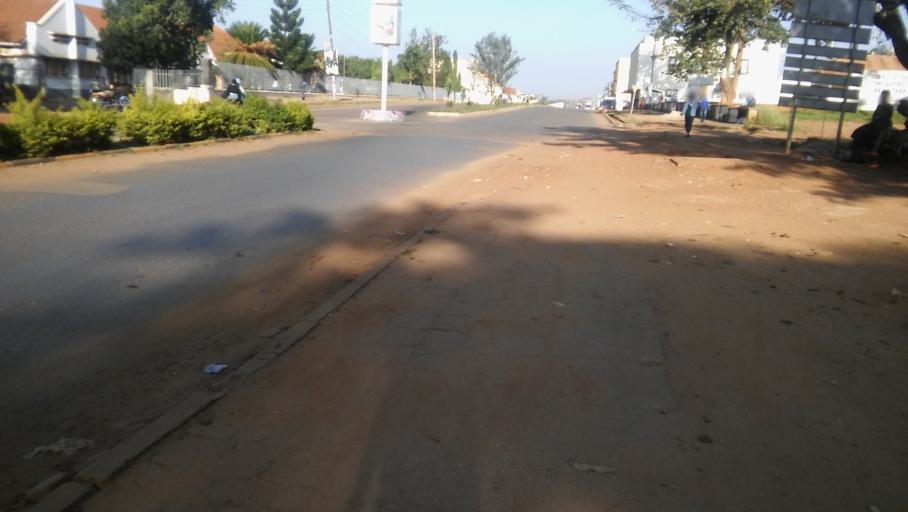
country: UG
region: Eastern Region
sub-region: Mbale District
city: Mbale
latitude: 1.0704
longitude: 34.1837
